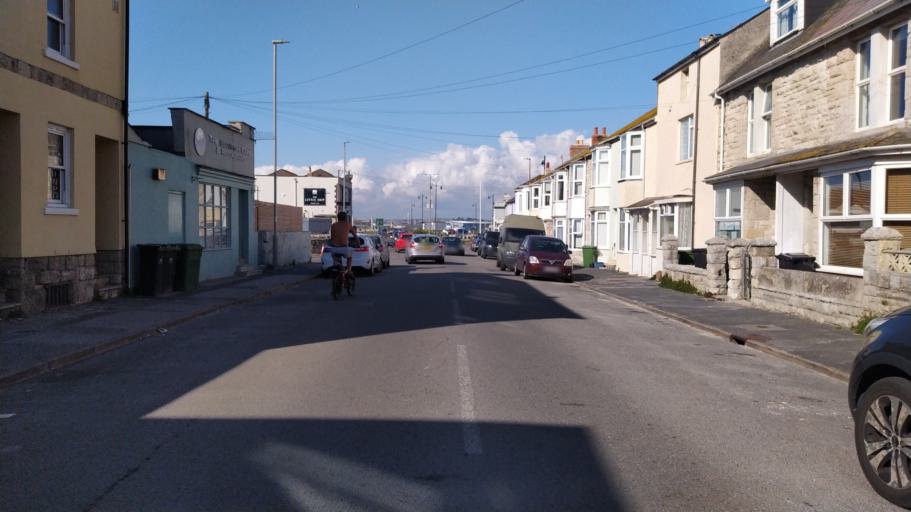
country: GB
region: England
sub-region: Dorset
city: Fortuneswell
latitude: 50.5620
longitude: -2.4487
